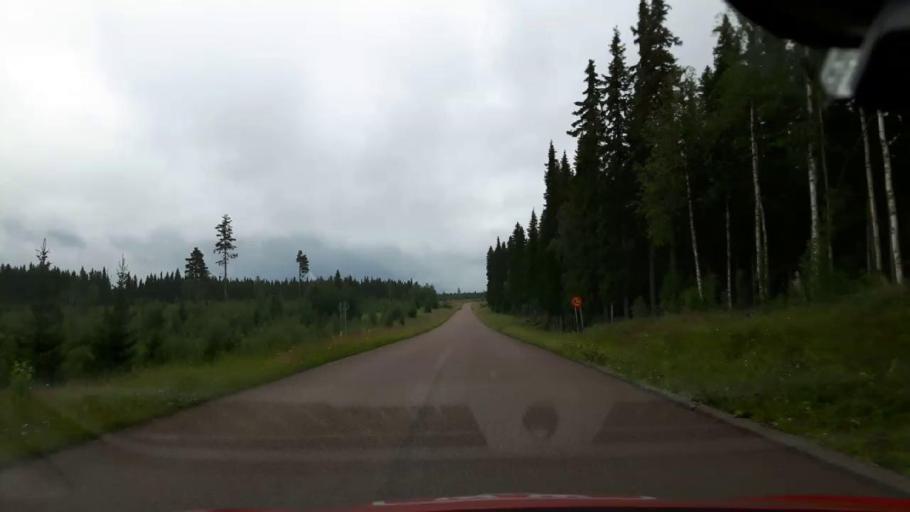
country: SE
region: Jaemtland
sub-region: Krokoms Kommun
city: Valla
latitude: 63.3794
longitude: 13.7585
